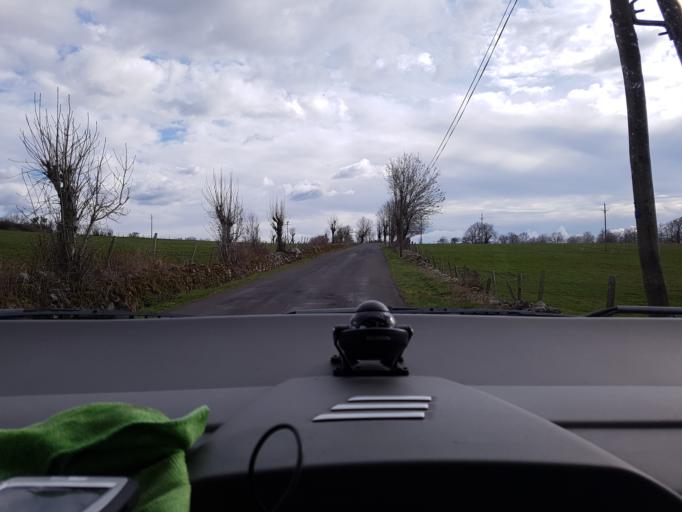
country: FR
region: Midi-Pyrenees
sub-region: Departement de l'Aveyron
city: Laguiole
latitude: 44.6982
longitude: 2.8412
